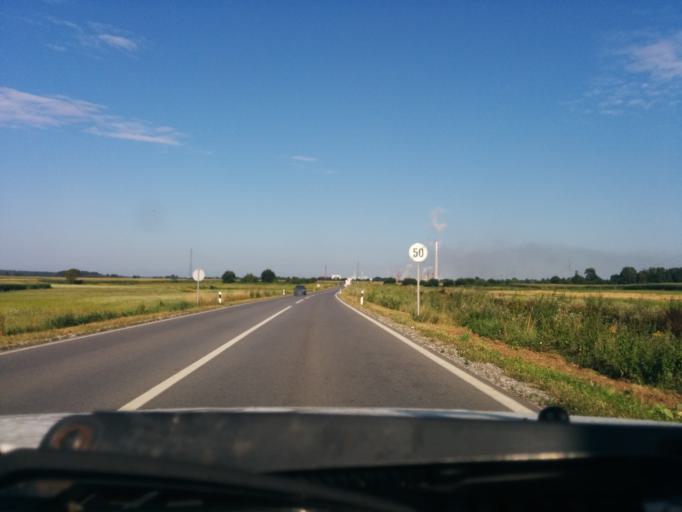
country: HR
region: Sisacko-Moslavacka
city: Husain
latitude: 45.4586
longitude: 16.8350
